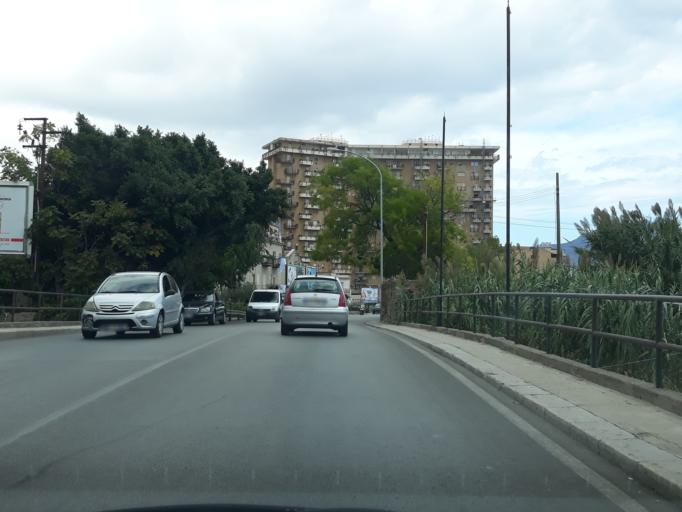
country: IT
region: Sicily
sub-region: Palermo
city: Ciaculli
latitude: 38.1096
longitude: 13.3794
